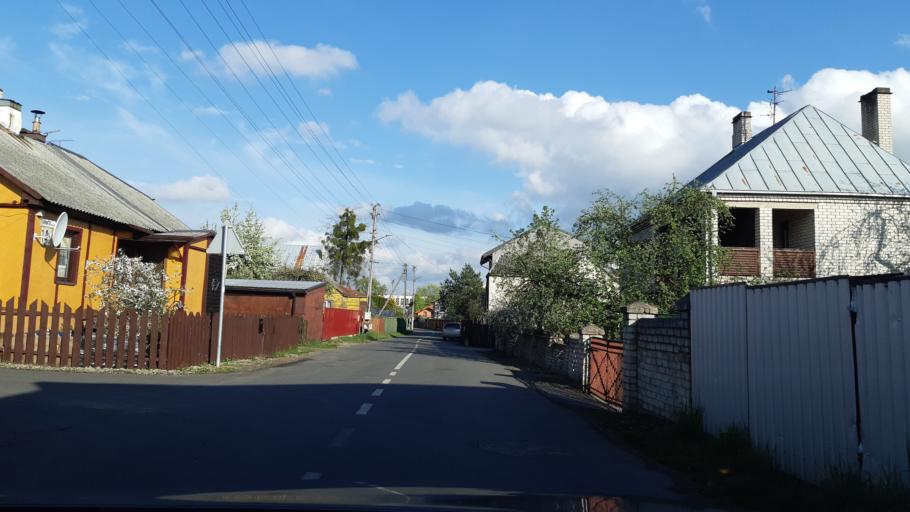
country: LT
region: Kauno apskritis
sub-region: Kaunas
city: Aleksotas
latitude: 54.8634
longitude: 23.9367
